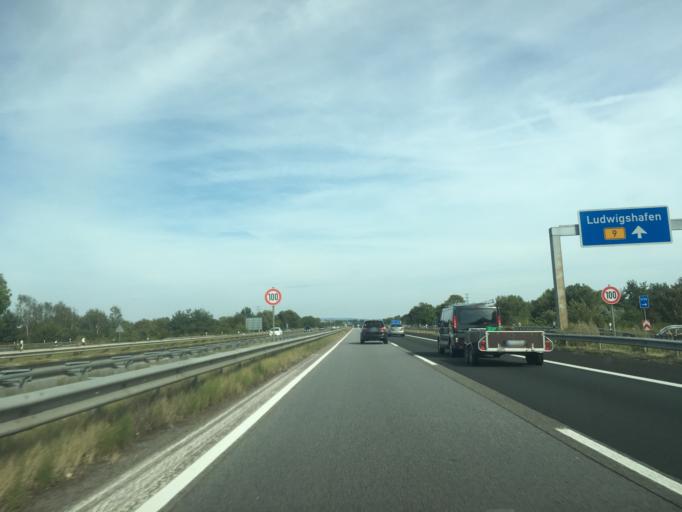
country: DE
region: Rheinland-Pfalz
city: Speyer
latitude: 49.3533
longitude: 8.4180
